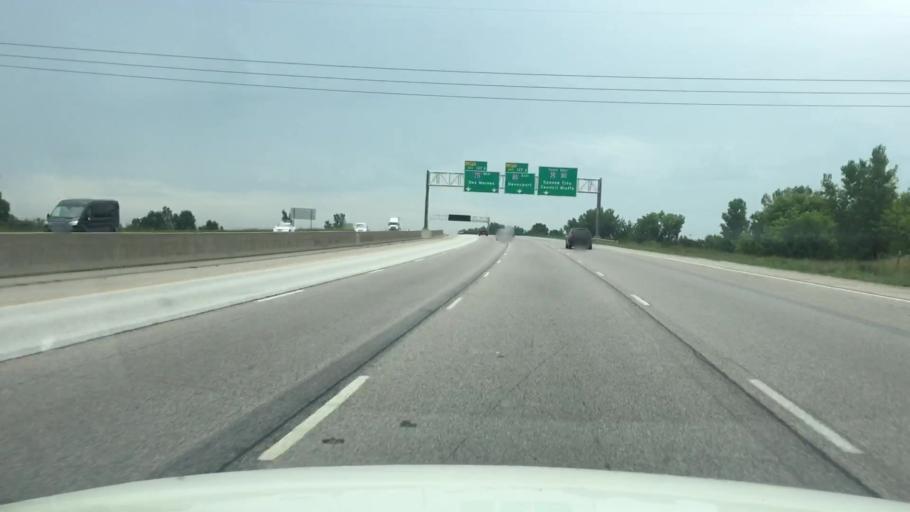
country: US
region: Iowa
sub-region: Polk County
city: Saylorville
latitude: 41.6735
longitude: -93.5781
